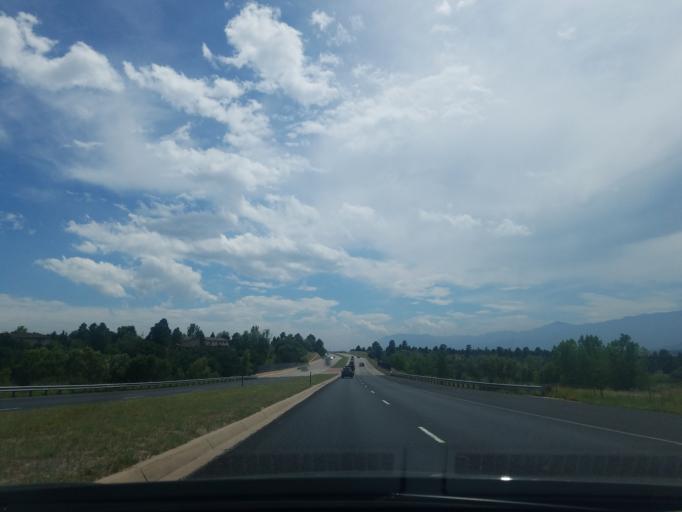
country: US
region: Colorado
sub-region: El Paso County
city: Air Force Academy
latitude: 38.9774
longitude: -104.7982
